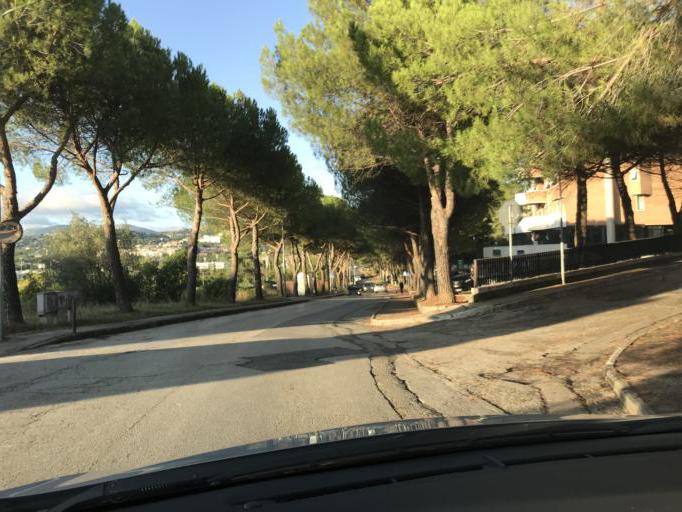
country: IT
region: Umbria
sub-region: Provincia di Perugia
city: Perugia
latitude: 43.1002
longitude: 12.3624
